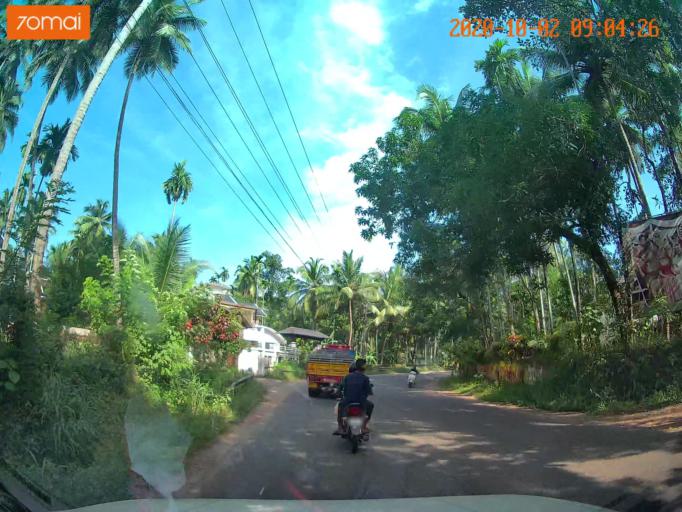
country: IN
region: Kerala
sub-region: Kozhikode
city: Naduvannur
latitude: 11.4767
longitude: 75.7748
